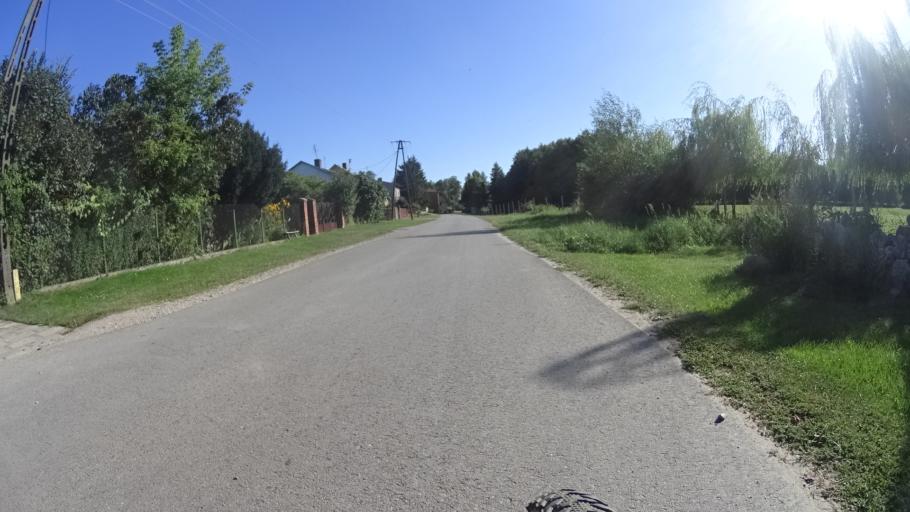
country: PL
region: Masovian Voivodeship
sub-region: Powiat bialobrzeski
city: Wysmierzyce
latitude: 51.6662
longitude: 20.8482
